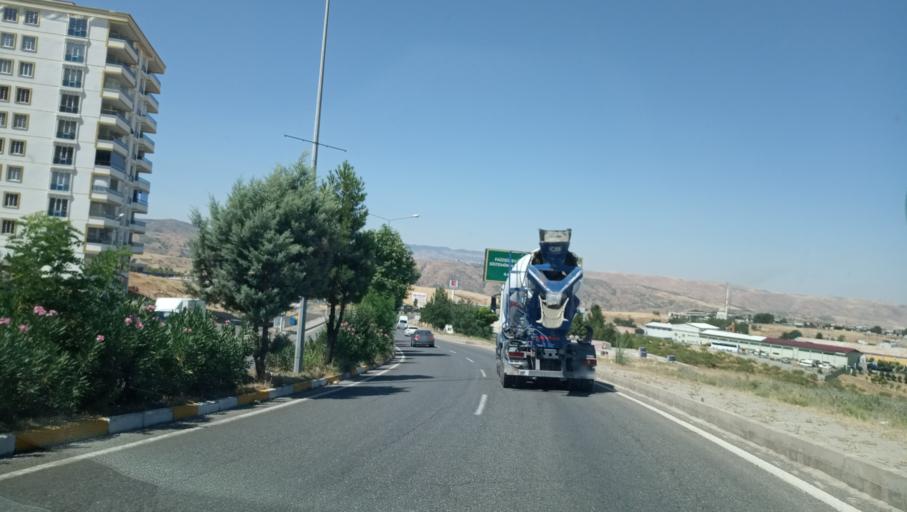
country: TR
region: Siirt
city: Civankan
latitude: 37.9529
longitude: 41.8869
